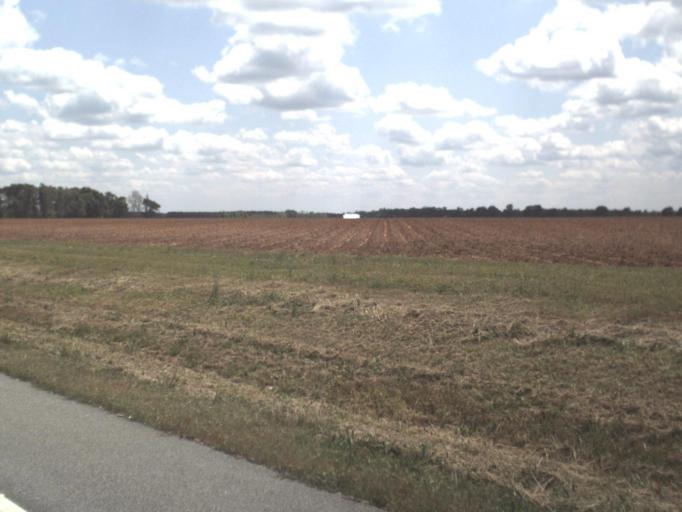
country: US
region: Alabama
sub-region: Escambia County
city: Atmore
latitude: 30.8830
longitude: -87.4487
